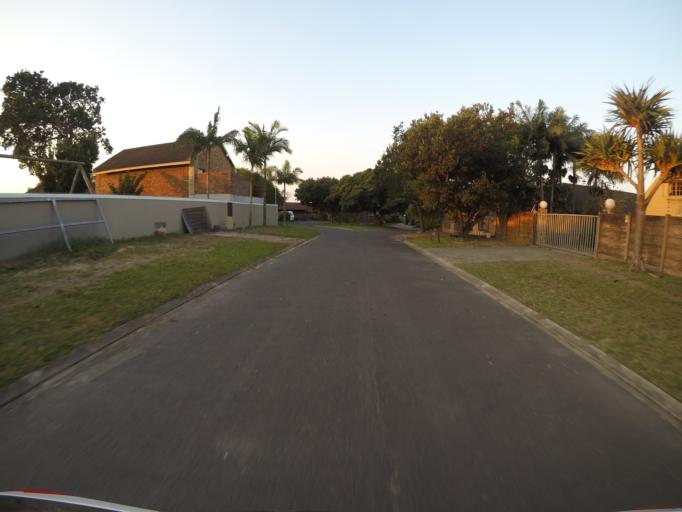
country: ZA
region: KwaZulu-Natal
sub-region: uThungulu District Municipality
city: Richards Bay
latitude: -28.7673
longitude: 32.1229
